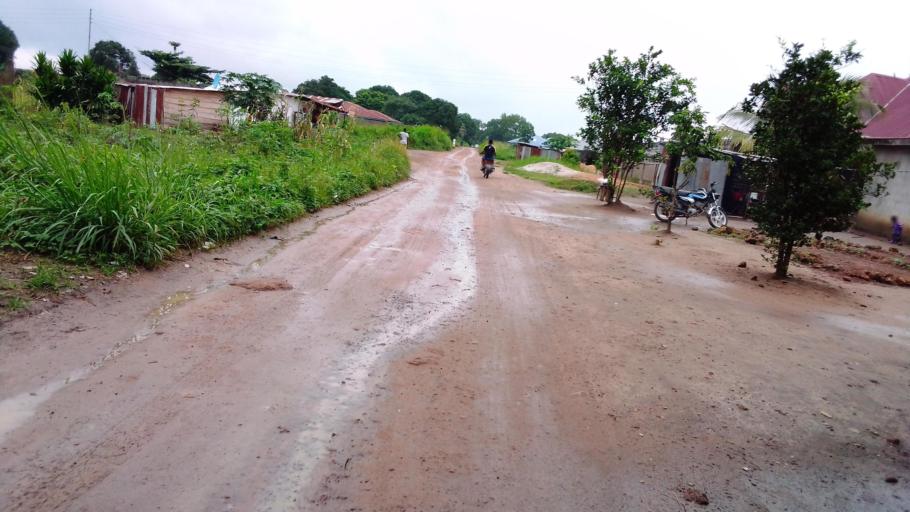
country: SL
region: Eastern Province
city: Kenema
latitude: 7.9011
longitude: -11.1683
